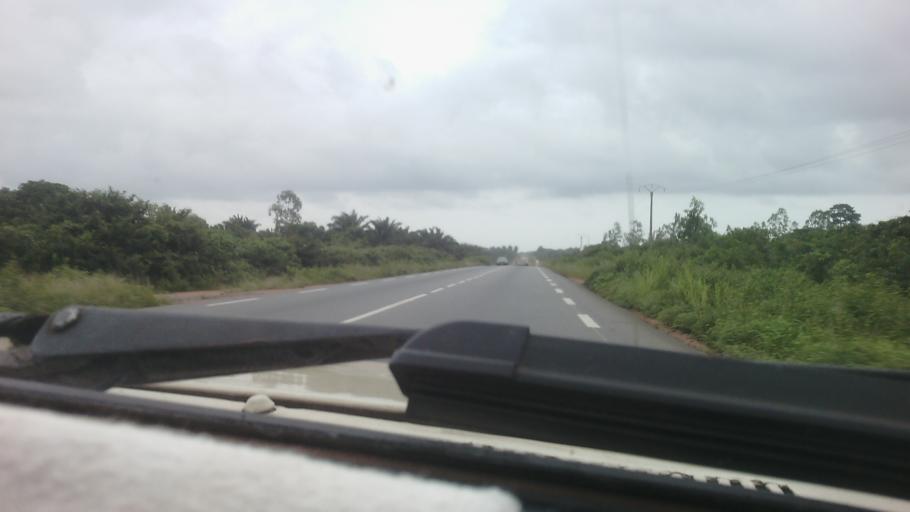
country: BJ
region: Atlantique
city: Ouidah
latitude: 6.3842
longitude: 2.0168
